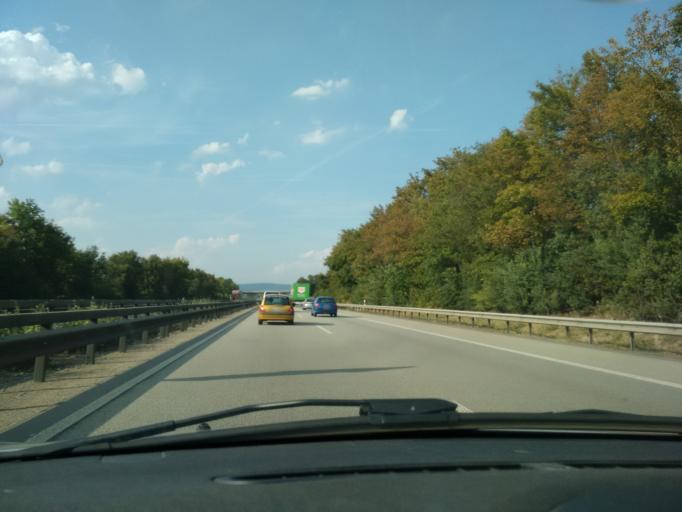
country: DE
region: Rheinland-Pfalz
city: Gensingen
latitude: 49.9021
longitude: 7.9465
